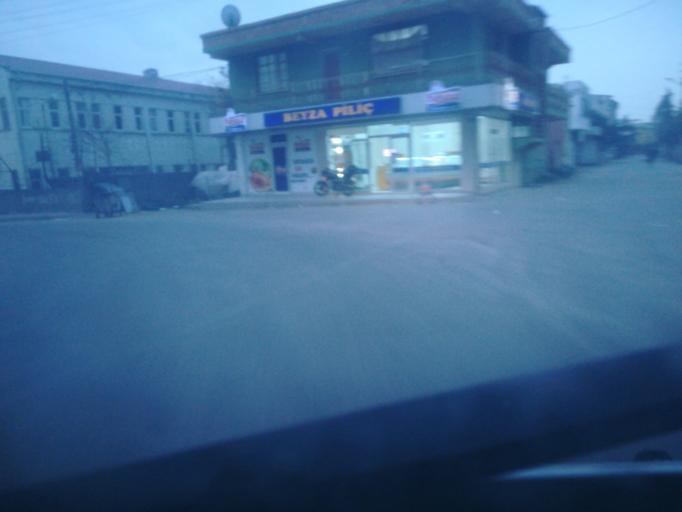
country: TR
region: Adana
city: Seyhan
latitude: 37.0141
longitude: 35.2823
